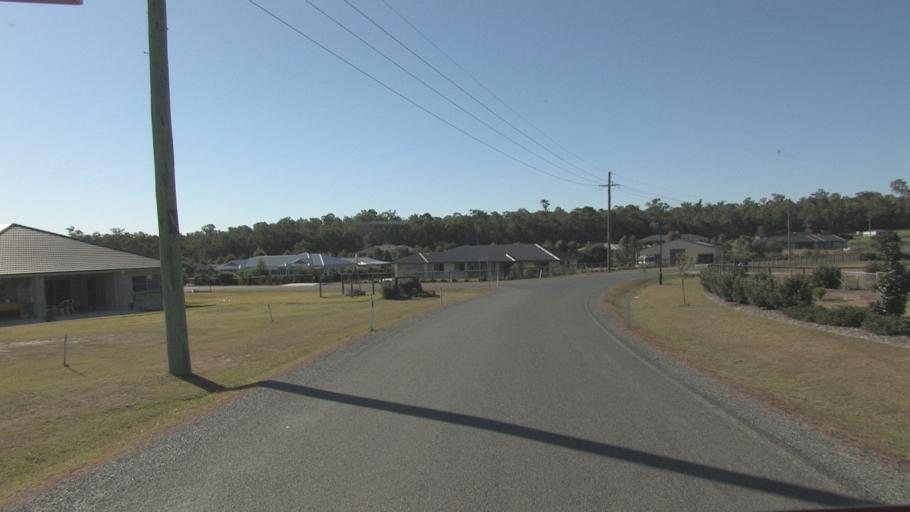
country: AU
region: Queensland
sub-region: Logan
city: Logan Reserve
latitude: -27.7503
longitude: 153.1353
